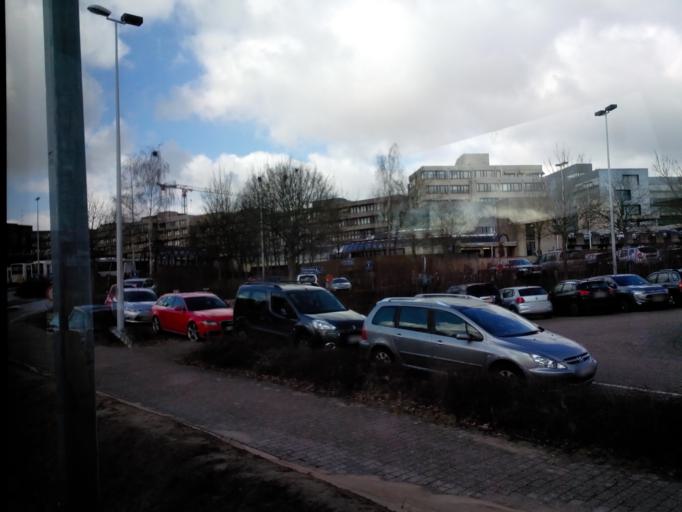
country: BE
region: Flanders
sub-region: Provincie Vlaams-Brabant
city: Leuven
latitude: 50.8789
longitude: 4.6767
